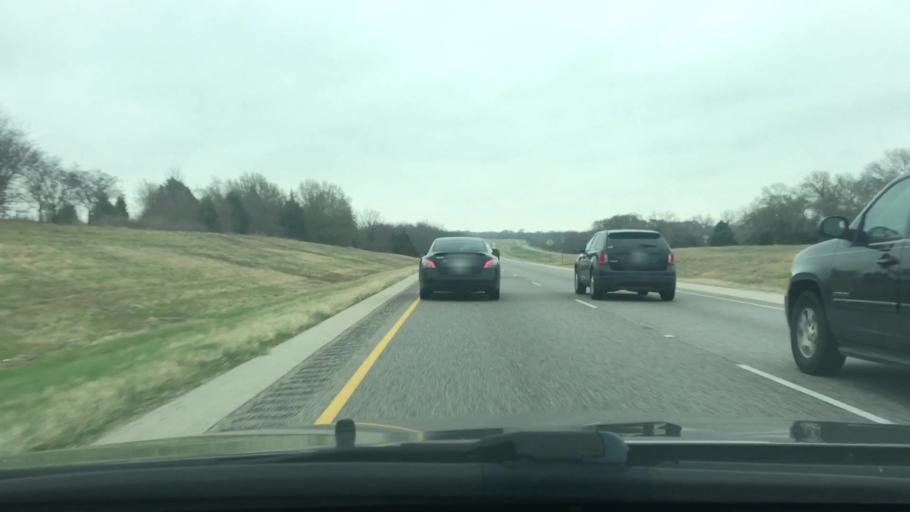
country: US
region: Texas
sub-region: Freestone County
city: Fairfield
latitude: 31.8031
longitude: -96.2614
